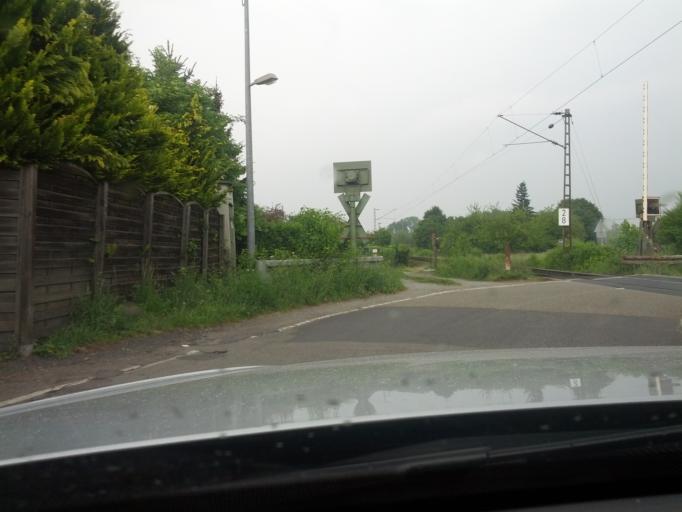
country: DE
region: Baden-Wuerttemberg
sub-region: Karlsruhe Region
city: Karlsruhe
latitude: 49.0123
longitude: 8.4499
